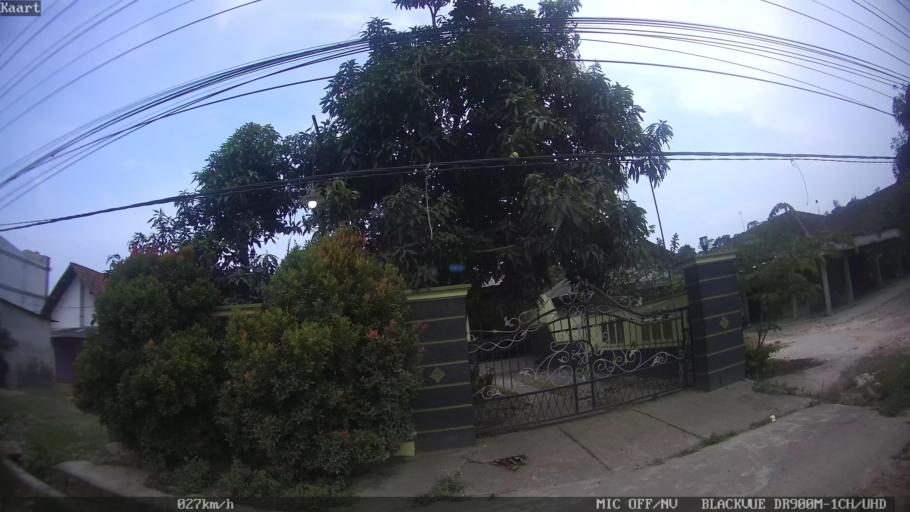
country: ID
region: Lampung
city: Panjang
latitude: -5.4188
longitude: 105.3359
